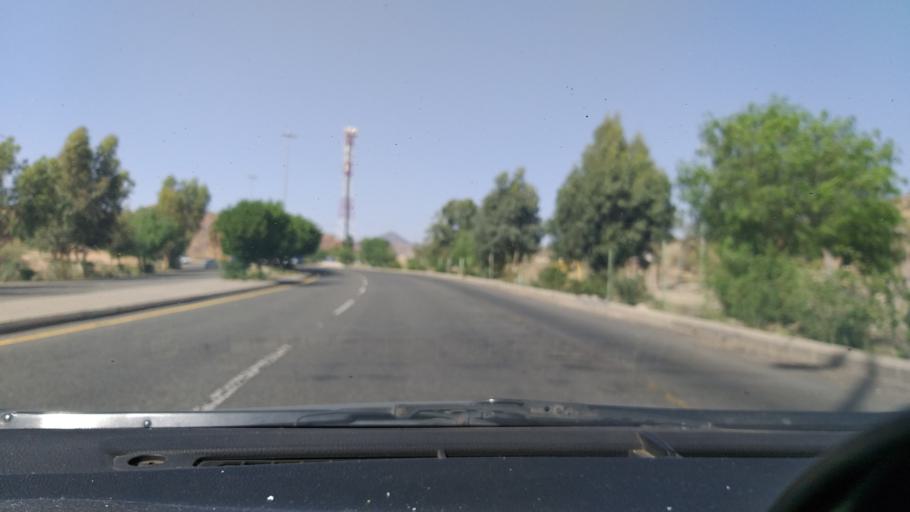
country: SA
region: Makkah
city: Ash Shafa
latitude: 21.1611
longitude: 40.3717
